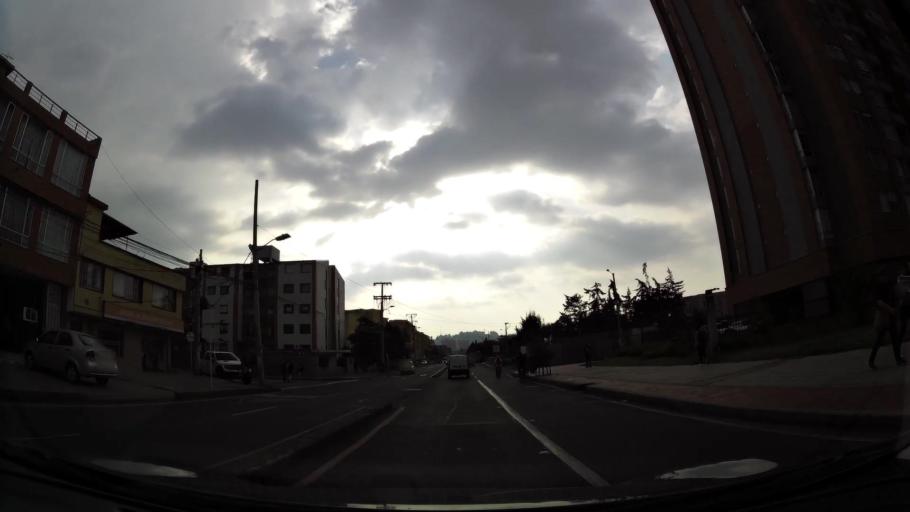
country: CO
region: Bogota D.C.
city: Barrio San Luis
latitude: 4.7165
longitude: -74.0612
